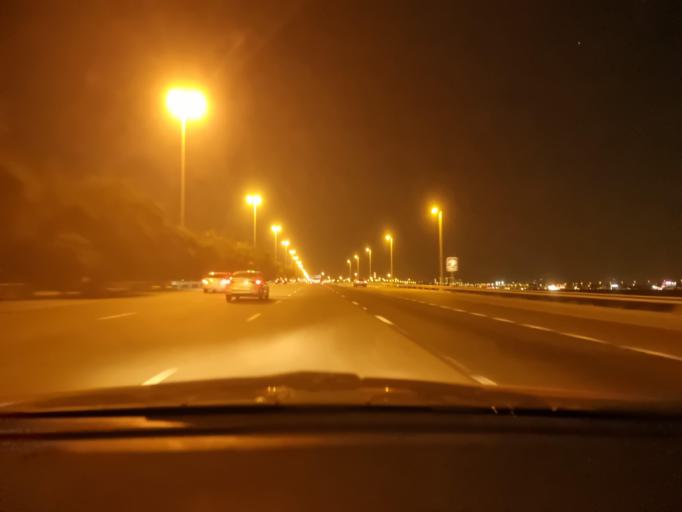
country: AE
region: Abu Dhabi
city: Abu Dhabi
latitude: 24.3500
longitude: 54.6439
